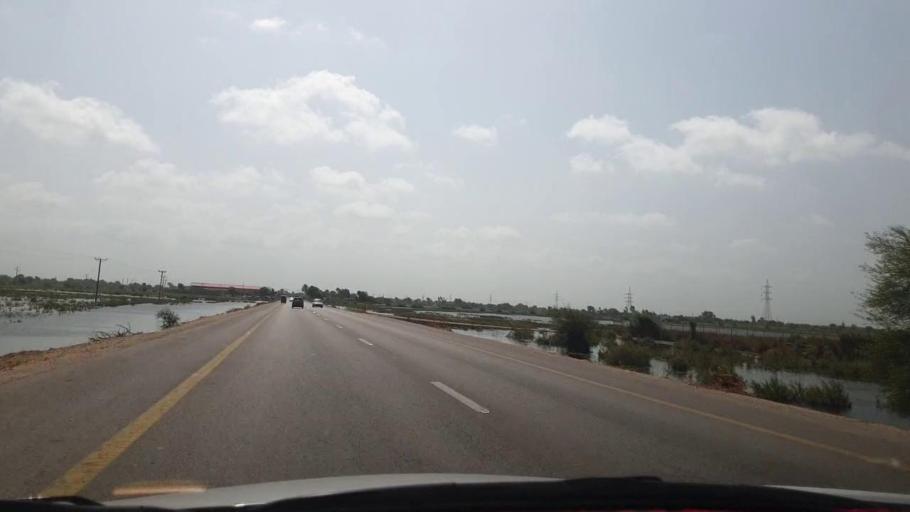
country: PK
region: Sindh
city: Talhar
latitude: 24.9166
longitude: 68.7270
